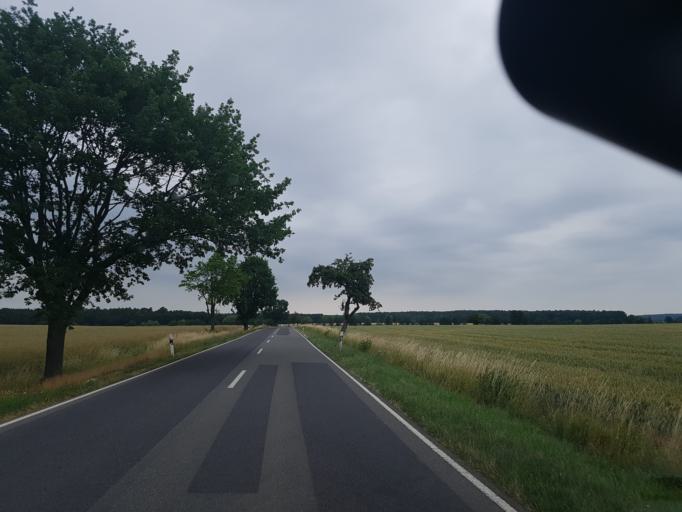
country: DE
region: Brandenburg
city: Lebusa
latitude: 51.8005
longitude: 13.4198
